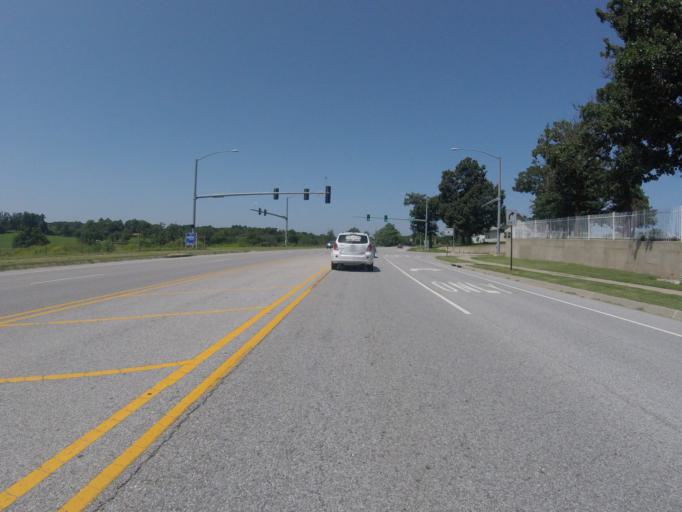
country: US
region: Arkansas
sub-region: Washington County
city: Farmington
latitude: 36.0928
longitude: -94.2123
